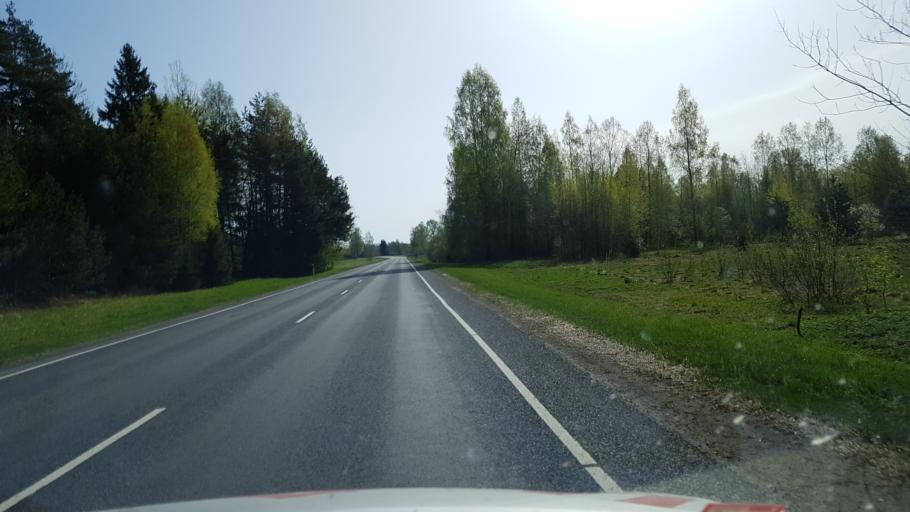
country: EE
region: Viljandimaa
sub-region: Abja vald
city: Abja-Paluoja
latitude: 58.1211
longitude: 25.3046
